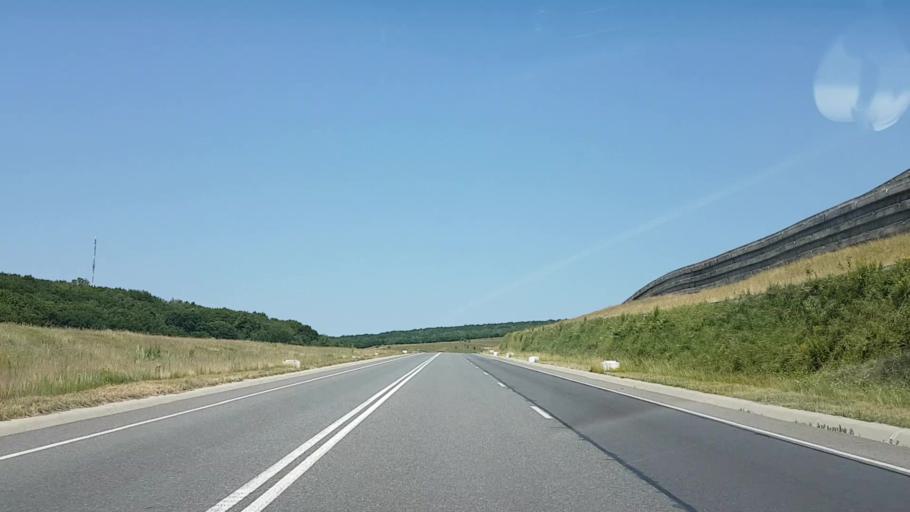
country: RO
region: Cluj
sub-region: Comuna Feleacu
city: Feleacu
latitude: 46.6984
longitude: 23.6382
